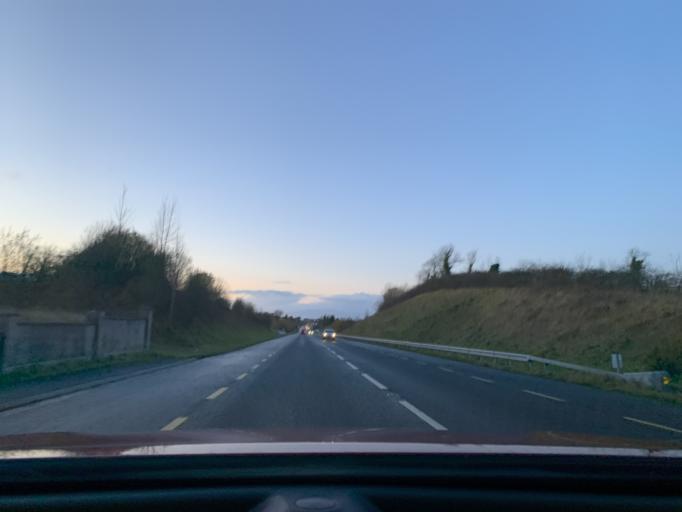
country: IE
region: Connaught
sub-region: County Leitrim
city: Carrick-on-Shannon
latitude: 53.9393
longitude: -8.0613
